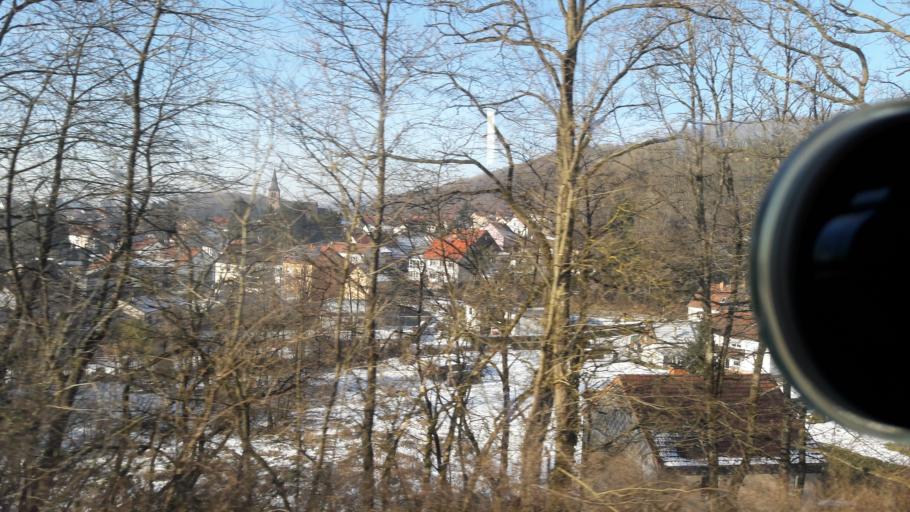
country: DE
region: Saarland
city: Namborn
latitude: 49.5218
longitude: 7.1466
